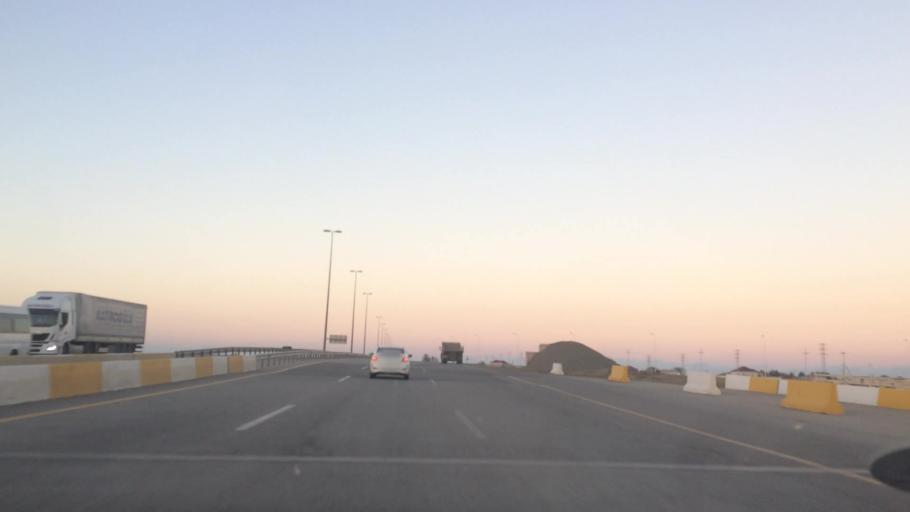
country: AZ
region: Baki
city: Qobustan
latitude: 39.9816
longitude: 49.4234
